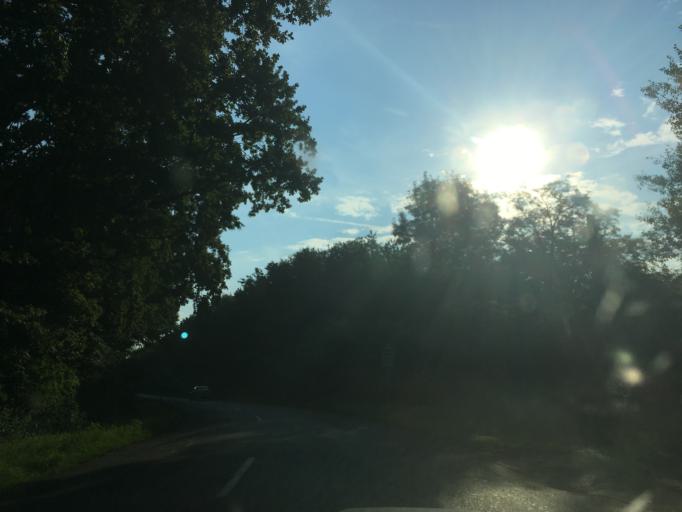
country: HU
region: Hajdu-Bihar
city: Hajdusamson
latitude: 47.5541
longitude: 21.7386
